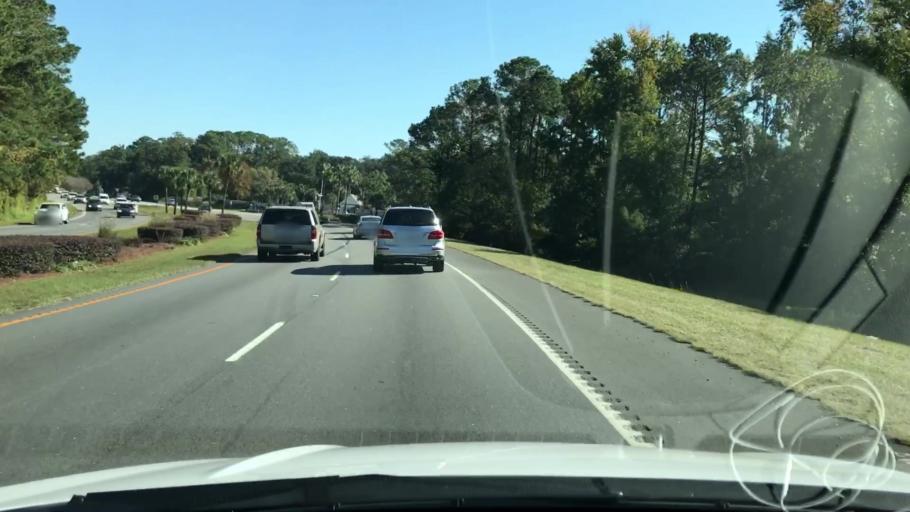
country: US
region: South Carolina
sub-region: Beaufort County
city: Hilton Head Island
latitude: 32.2186
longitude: -80.7758
